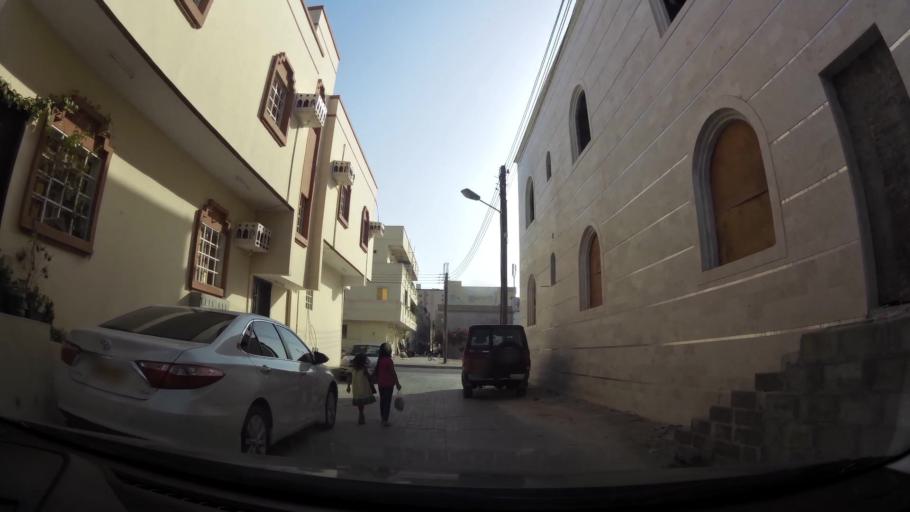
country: OM
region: Zufar
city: Salalah
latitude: 17.0122
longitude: 54.0840
